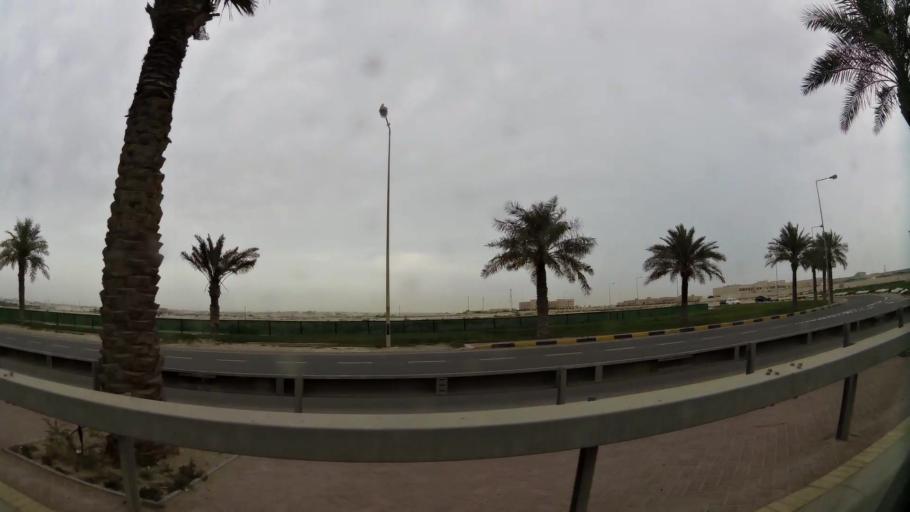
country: BH
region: Northern
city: Ar Rifa'
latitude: 26.1028
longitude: 50.5423
